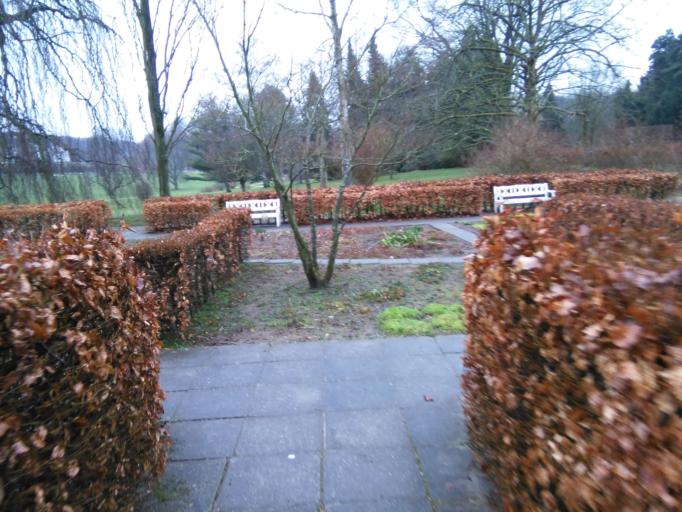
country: DK
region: Central Jutland
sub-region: Arhus Kommune
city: Arhus
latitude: 56.1312
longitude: 10.2071
